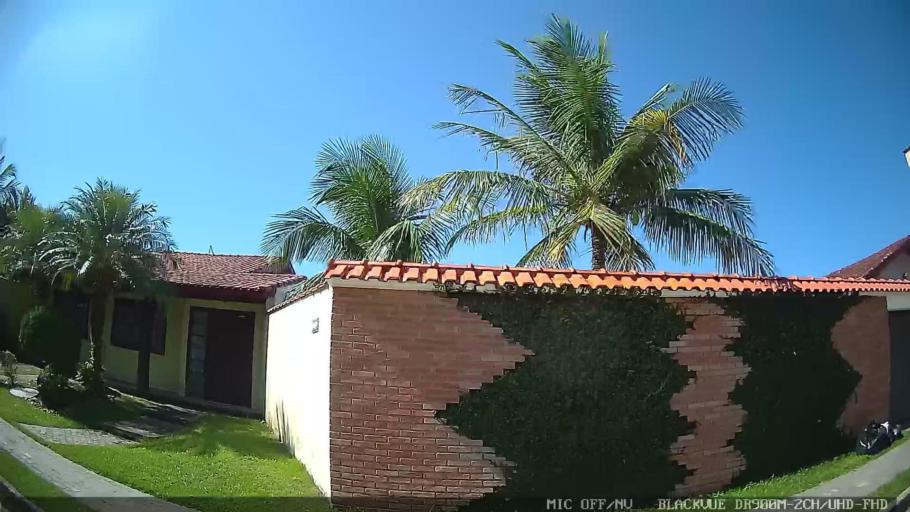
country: BR
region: Sao Paulo
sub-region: Peruibe
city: Peruibe
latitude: -24.2980
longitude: -46.9719
